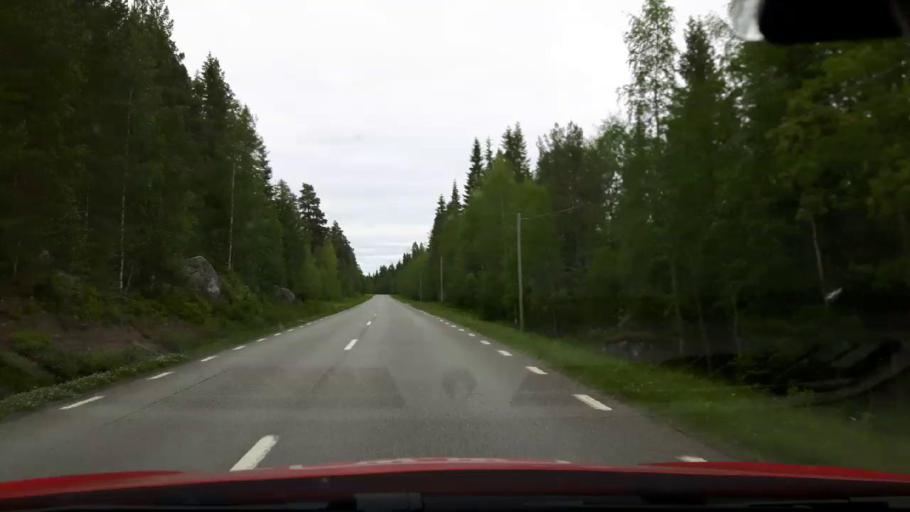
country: SE
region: Jaemtland
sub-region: Stroemsunds Kommun
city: Stroemsund
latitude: 63.4015
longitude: 15.6287
